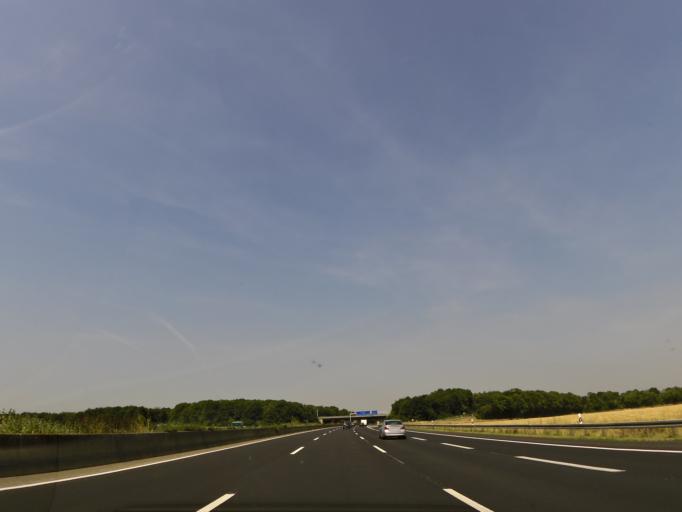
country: DE
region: North Rhine-Westphalia
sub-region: Regierungsbezirk Koln
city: Weilerswist
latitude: 50.7680
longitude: 6.8302
